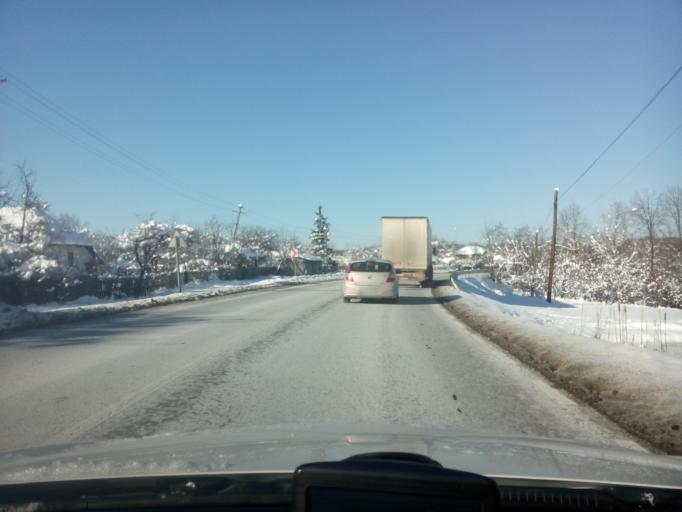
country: RO
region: Arges
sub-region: Comuna Cotmeana
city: Cotmeana
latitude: 44.9839
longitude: 24.6494
